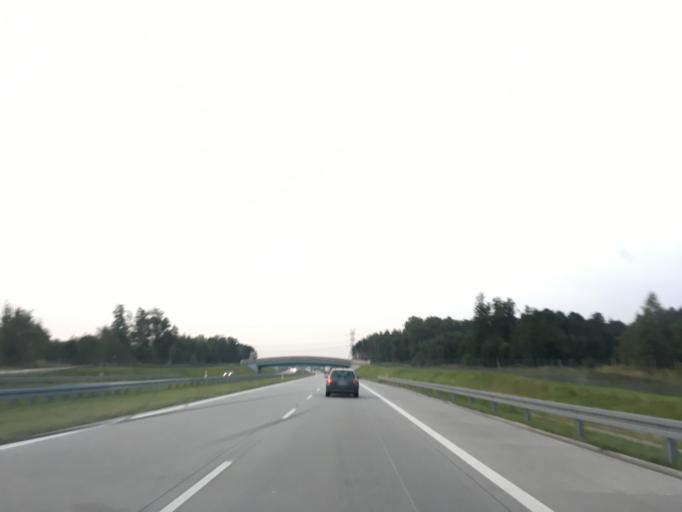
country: PL
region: Lodz Voivodeship
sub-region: Powiat lodzki wschodni
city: Tuszyn
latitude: 51.6084
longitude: 19.5739
